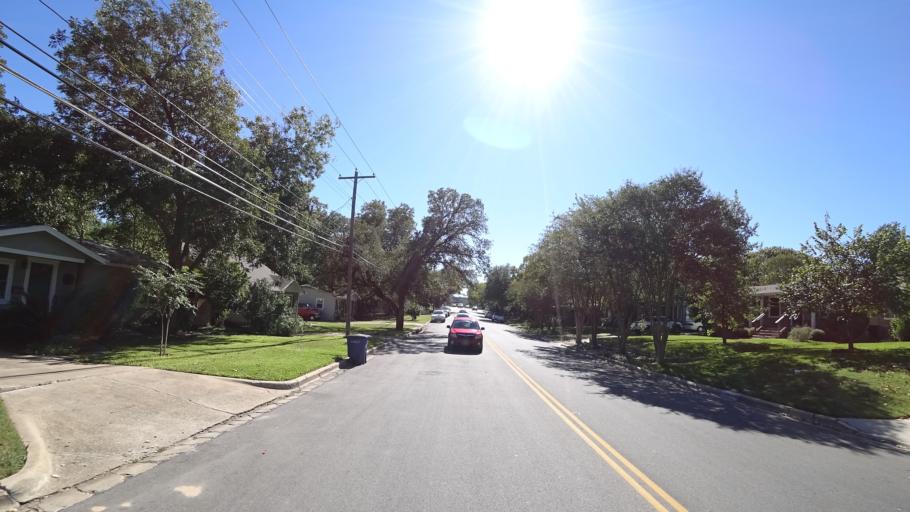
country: US
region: Texas
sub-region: Travis County
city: West Lake Hills
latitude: 30.3216
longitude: -97.7528
